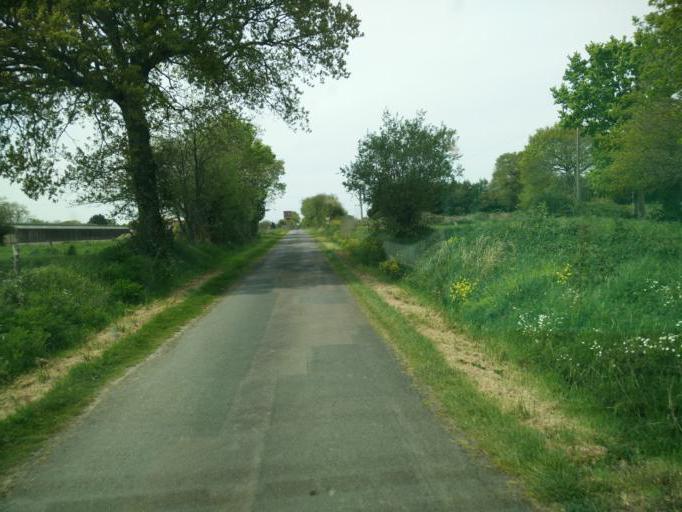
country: FR
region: Brittany
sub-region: Departement des Cotes-d'Armor
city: Matignon
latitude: 48.5861
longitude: -2.2506
